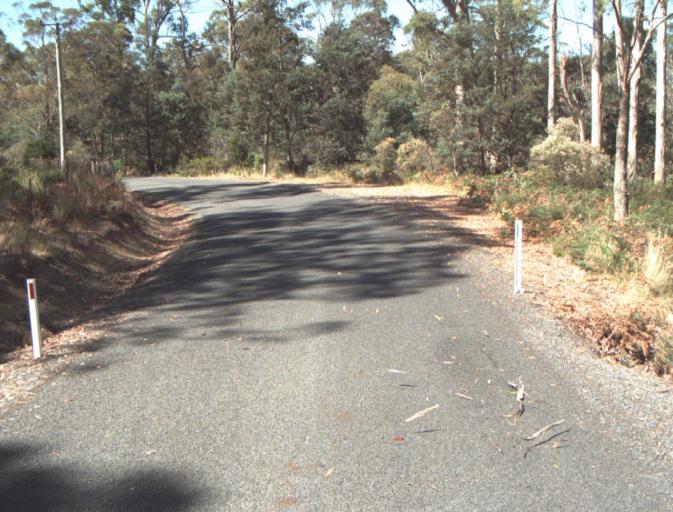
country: AU
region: Tasmania
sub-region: Launceston
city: Newstead
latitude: -41.3620
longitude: 147.3024
